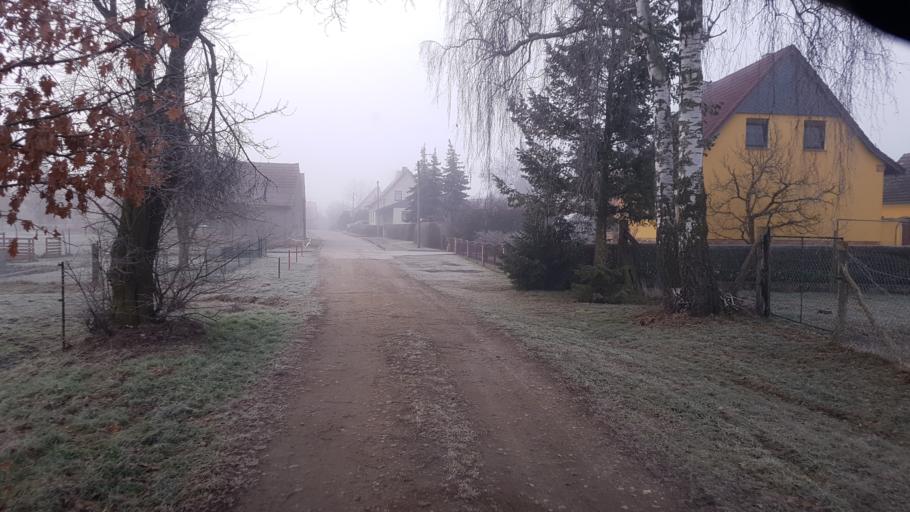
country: DE
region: Brandenburg
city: Ihlow
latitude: 51.8088
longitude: 13.3038
